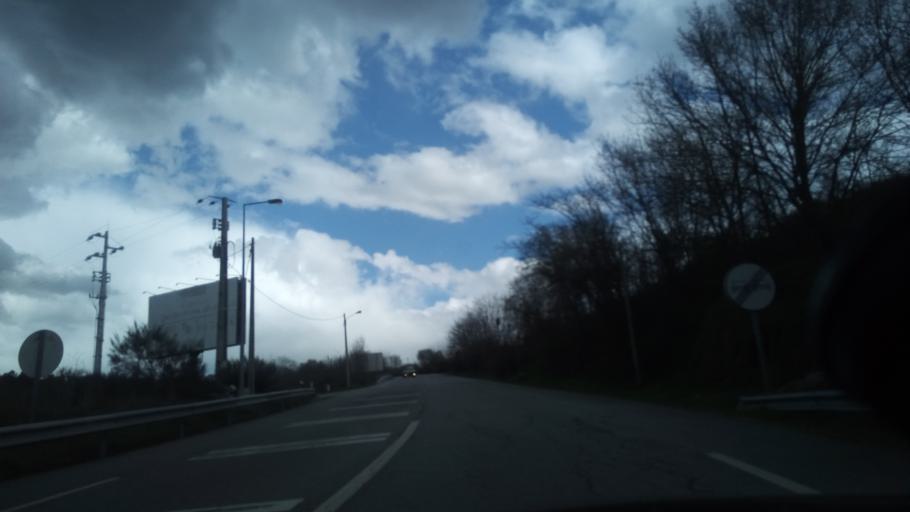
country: PT
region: Guarda
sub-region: Celorico da Beira
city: Celorico da Beira
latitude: 40.6301
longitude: -7.4123
